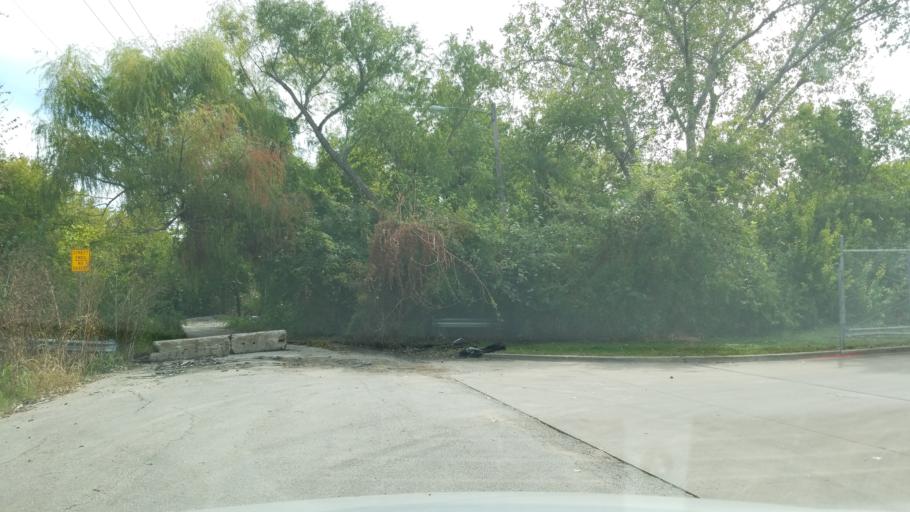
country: US
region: Texas
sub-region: Dallas County
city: Dallas
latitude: 32.7788
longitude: -96.7239
